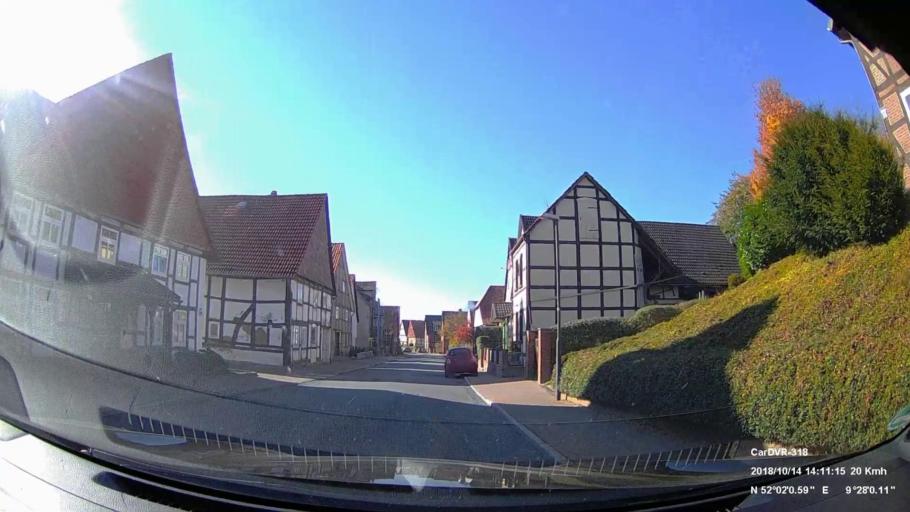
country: DE
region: Lower Saxony
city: Heyen
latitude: 52.0335
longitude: 9.4666
